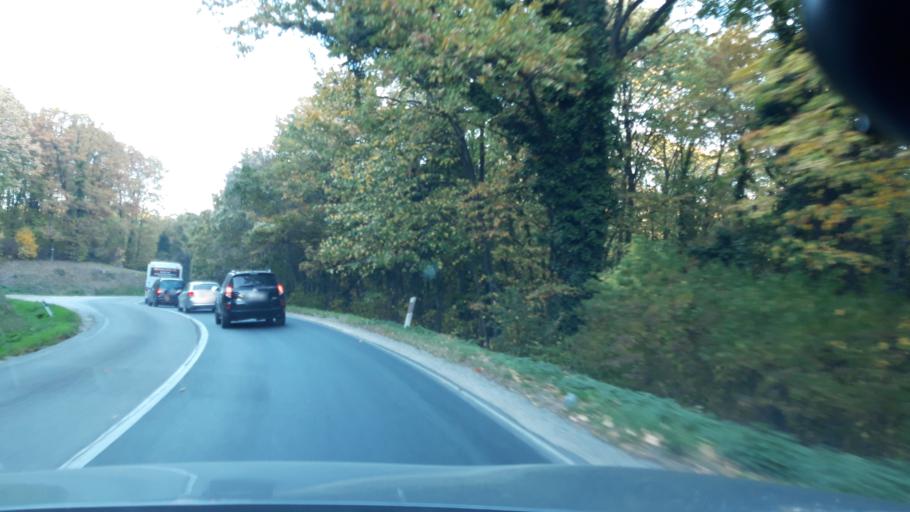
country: RS
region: Autonomna Pokrajina Vojvodina
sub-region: Sremski Okrug
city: Irig
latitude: 45.1442
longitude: 19.8371
